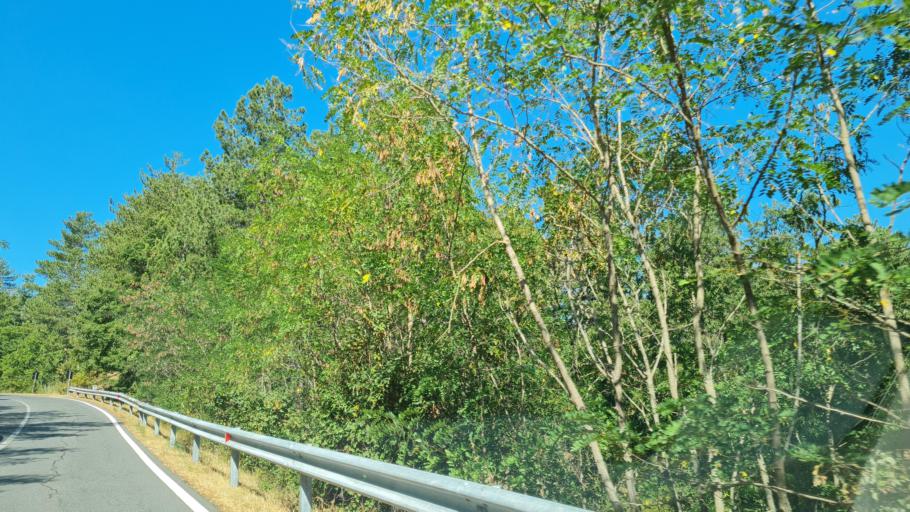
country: IT
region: Tuscany
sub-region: Provincia di Siena
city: Abbadia San Salvatore
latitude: 42.9125
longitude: 11.6846
